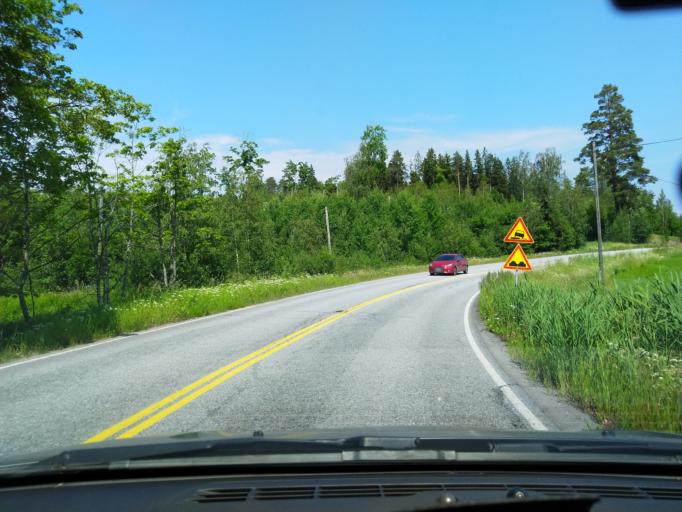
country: FI
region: Uusimaa
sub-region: Helsinki
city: Lohja
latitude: 60.3002
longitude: 24.0919
